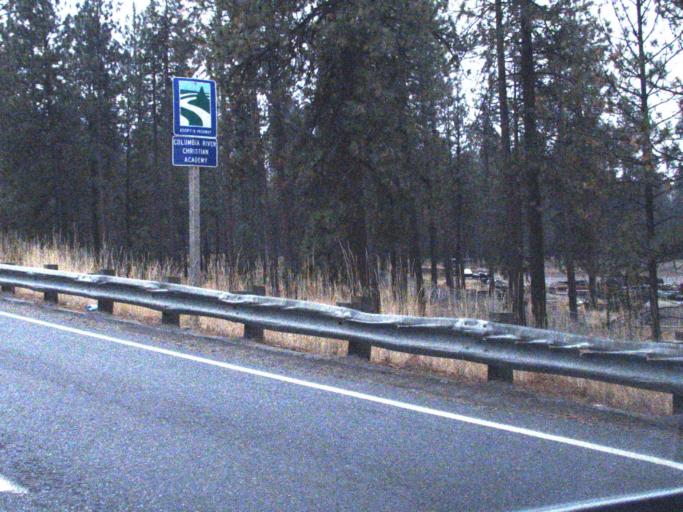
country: US
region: Washington
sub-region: Stevens County
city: Kettle Falls
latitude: 48.6195
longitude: -118.1077
